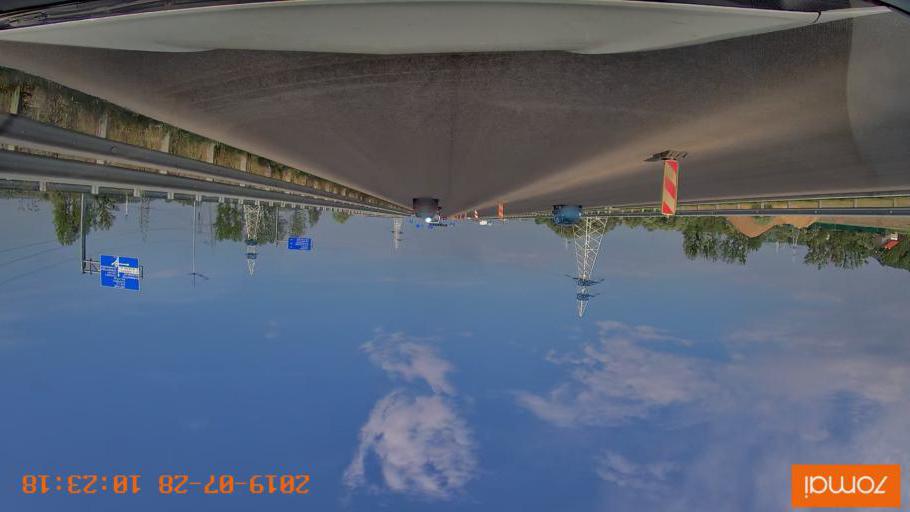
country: RU
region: Kaliningrad
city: Maloye Isakovo
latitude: 54.7660
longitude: 20.5612
